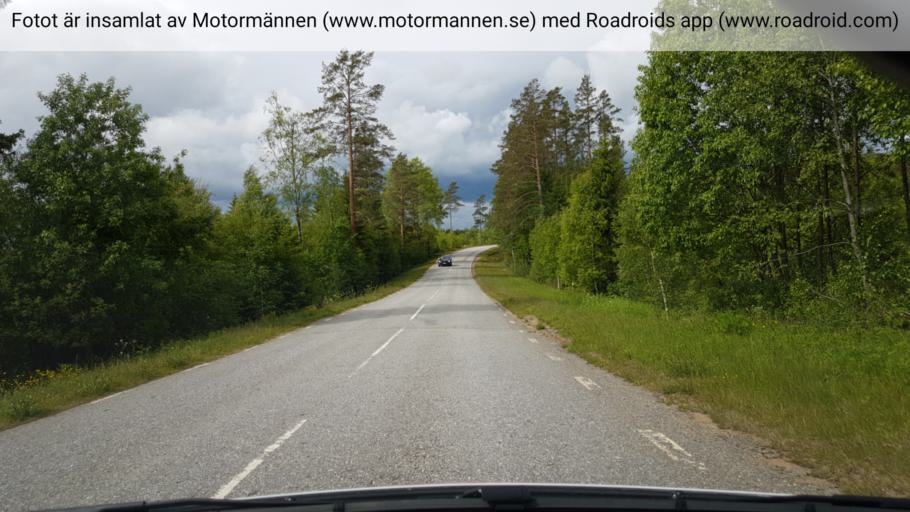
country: SE
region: Vaesterbotten
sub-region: Umea Kommun
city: Hoernefors
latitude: 63.5614
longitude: 19.7483
